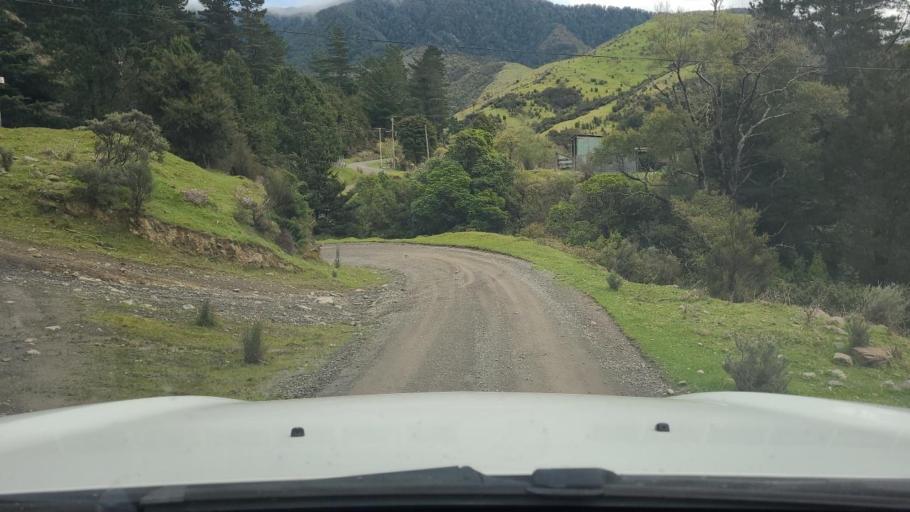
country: NZ
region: Wellington
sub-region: South Wairarapa District
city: Waipawa
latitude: -41.3885
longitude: 175.3736
